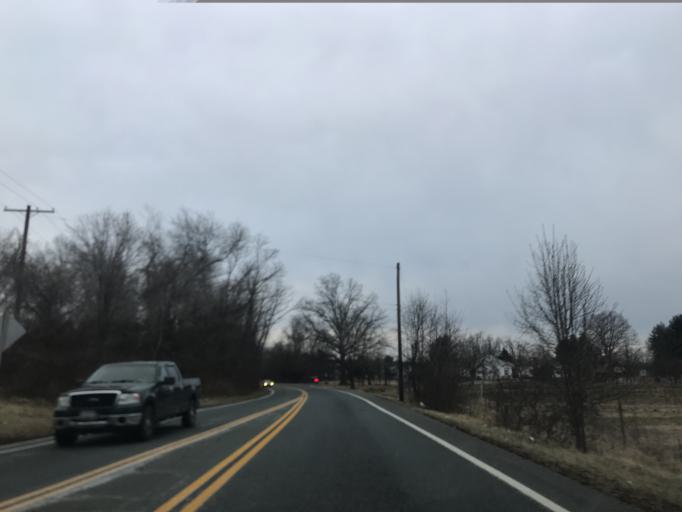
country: US
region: Maryland
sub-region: Prince George's County
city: Woodmore
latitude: 38.9067
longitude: -76.7975
